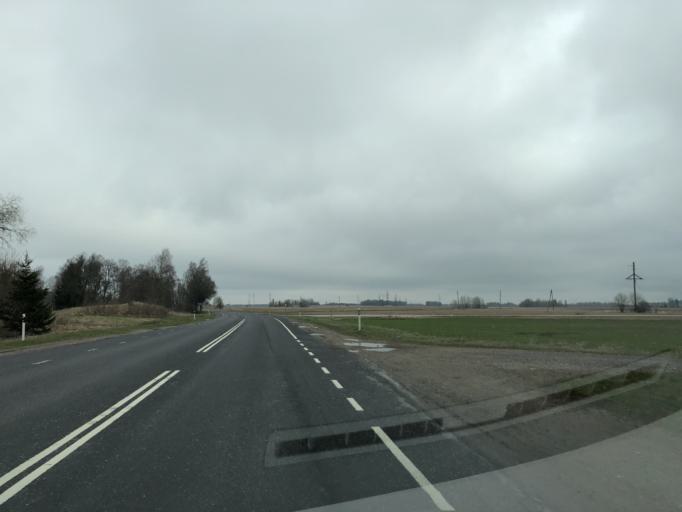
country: EE
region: Laeaene-Virumaa
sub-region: Vaeike-Maarja vald
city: Vaike-Maarja
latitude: 59.2088
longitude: 26.2701
